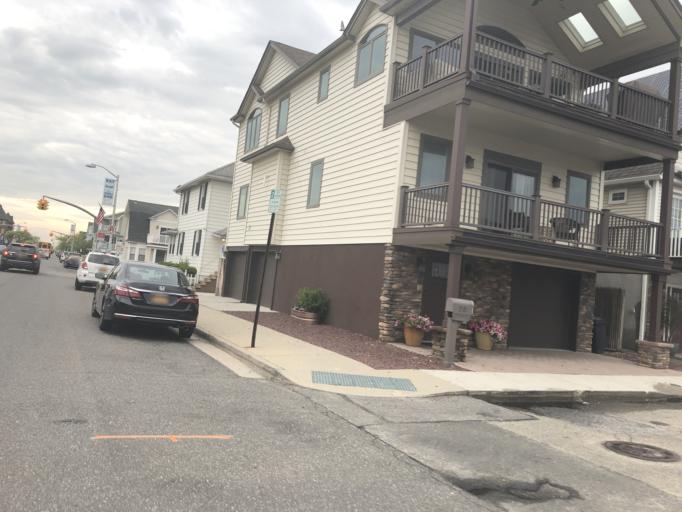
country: US
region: New York
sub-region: Nassau County
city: Harbor Isle
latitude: 40.5861
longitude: -73.6884
